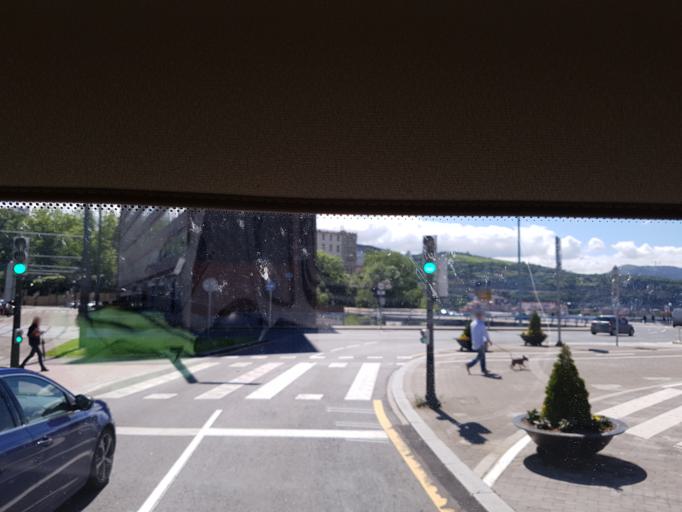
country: ES
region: Basque Country
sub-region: Bizkaia
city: Bilbao
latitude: 43.2661
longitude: -2.9447
